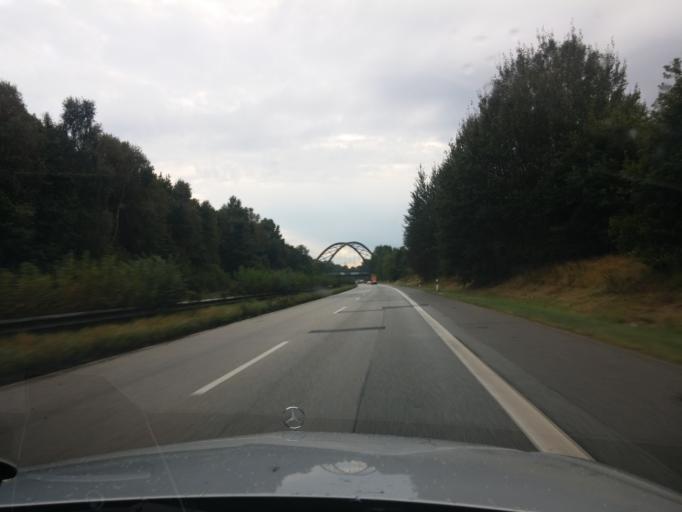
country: DE
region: Mecklenburg-Vorpommern
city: Selmsdorf
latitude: 53.9232
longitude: 10.8131
